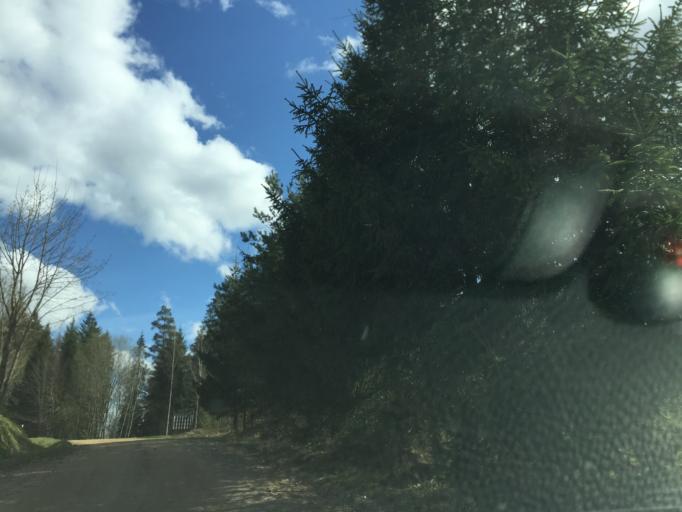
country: LV
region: Rezekne
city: Rezekne
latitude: 56.6569
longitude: 27.2732
